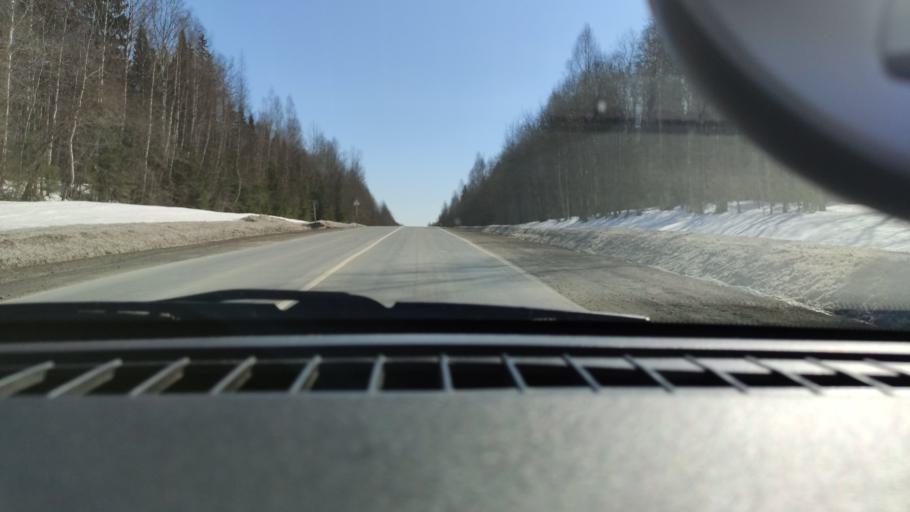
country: RU
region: Perm
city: Perm
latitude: 58.1540
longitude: 56.2531
